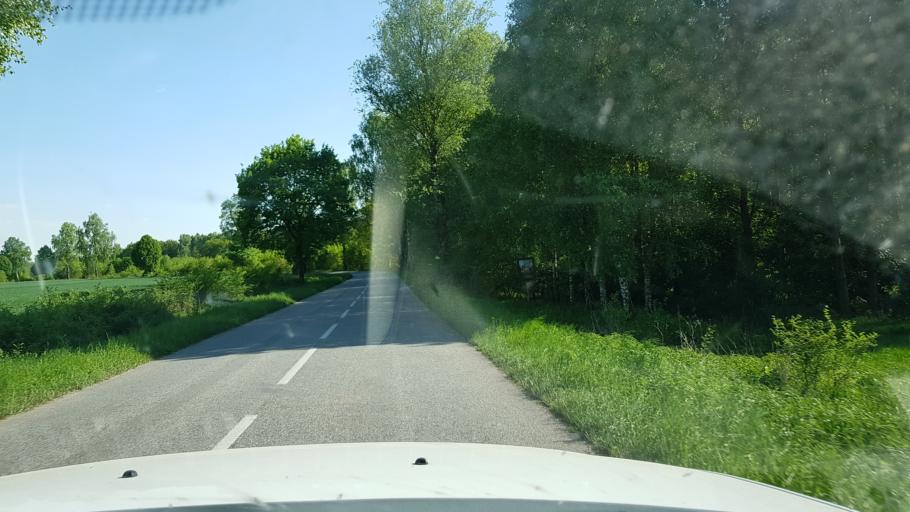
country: PL
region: West Pomeranian Voivodeship
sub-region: Powiat lobeski
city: Resko
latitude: 53.8185
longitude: 15.3962
